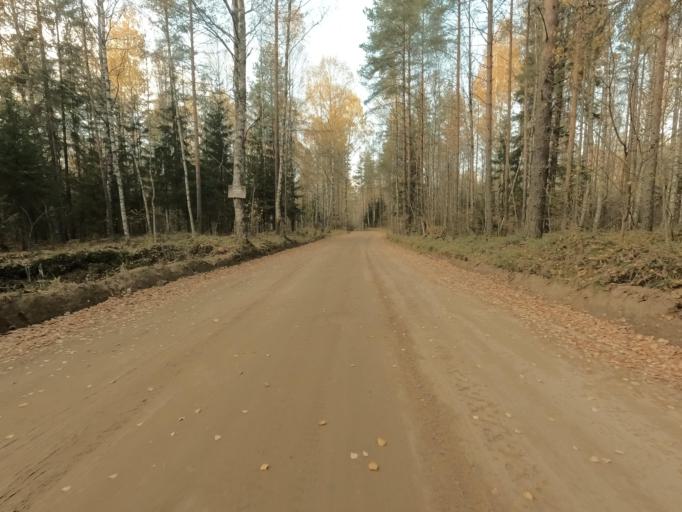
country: RU
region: Leningrad
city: Priladozhskiy
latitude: 59.7410
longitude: 31.3142
